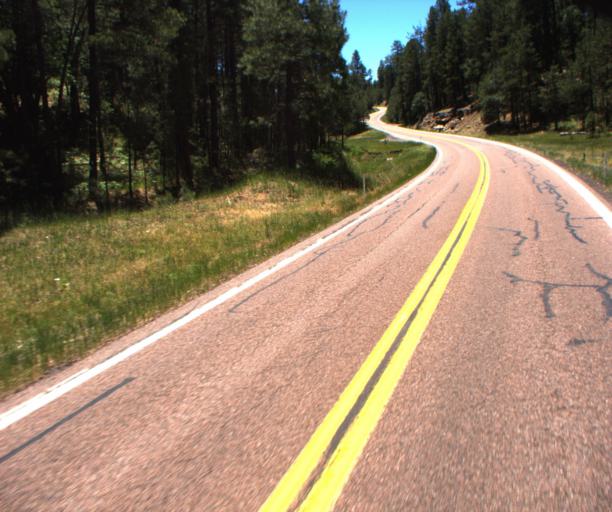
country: US
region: Arizona
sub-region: Gila County
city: Pine
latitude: 34.4987
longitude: -111.3679
